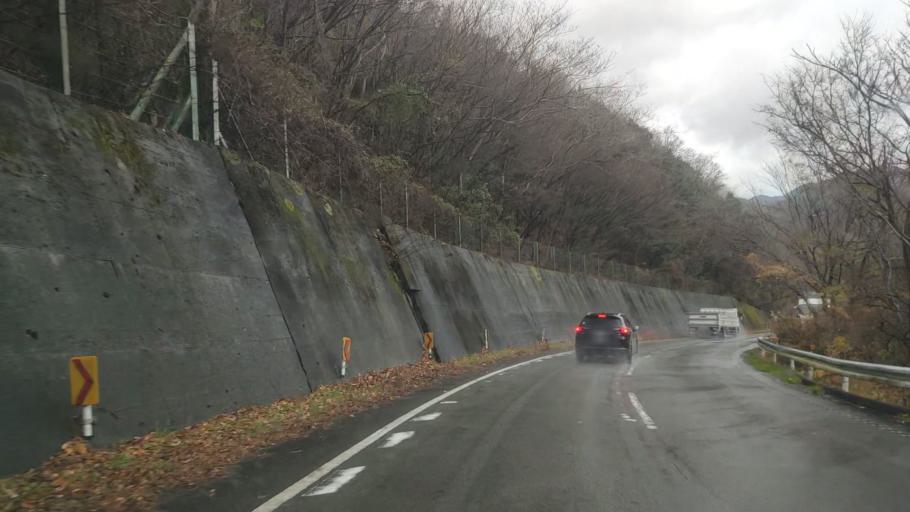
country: JP
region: Tokushima
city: Kamojimacho-jogejima
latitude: 34.1657
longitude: 134.3397
